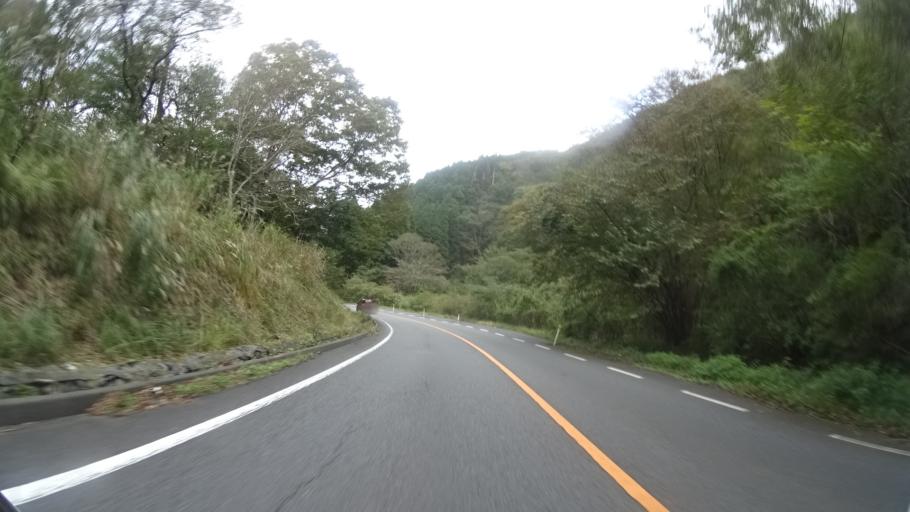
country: JP
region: Oita
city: Beppu
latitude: 33.2680
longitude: 131.4067
